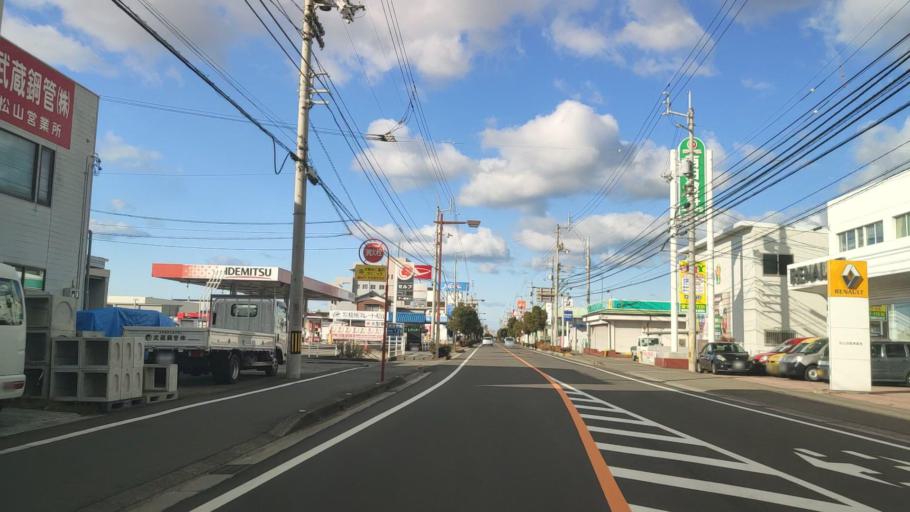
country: JP
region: Ehime
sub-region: Shikoku-chuo Shi
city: Matsuyama
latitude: 33.8285
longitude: 132.7424
